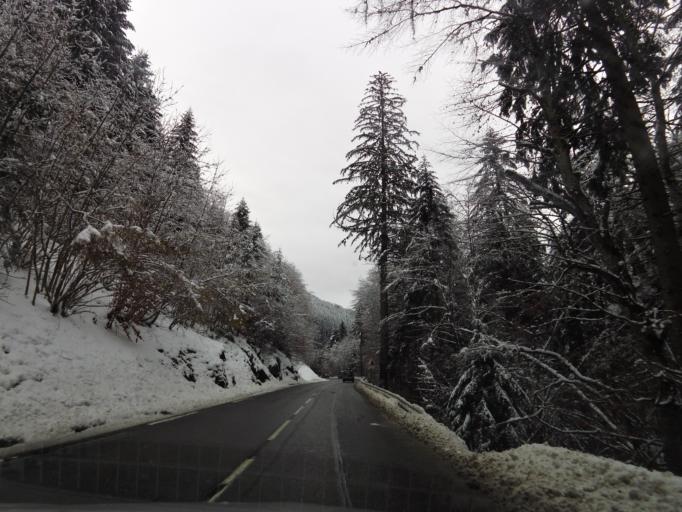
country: FR
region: Rhone-Alpes
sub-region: Departement de la Haute-Savoie
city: Taninges
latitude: 46.1305
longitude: 6.6240
